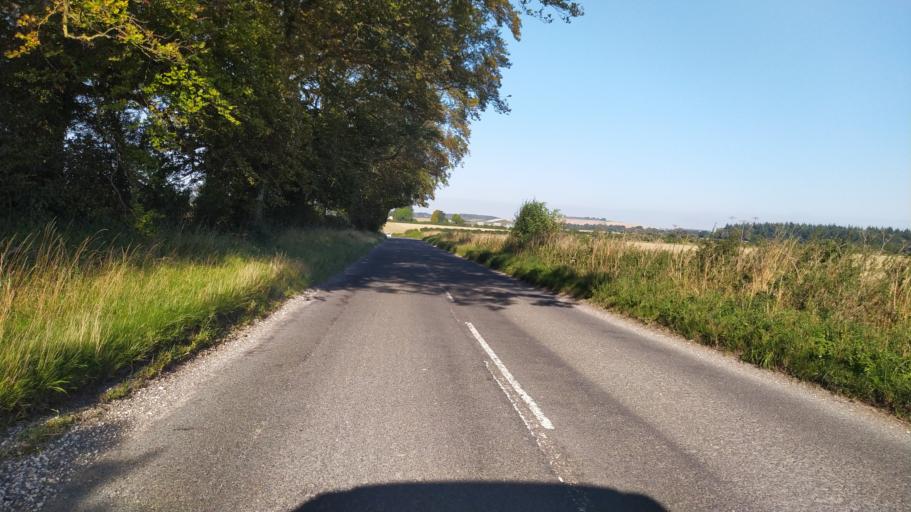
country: GB
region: England
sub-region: Hampshire
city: Abbotts Ann
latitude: 51.1613
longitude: -1.5708
